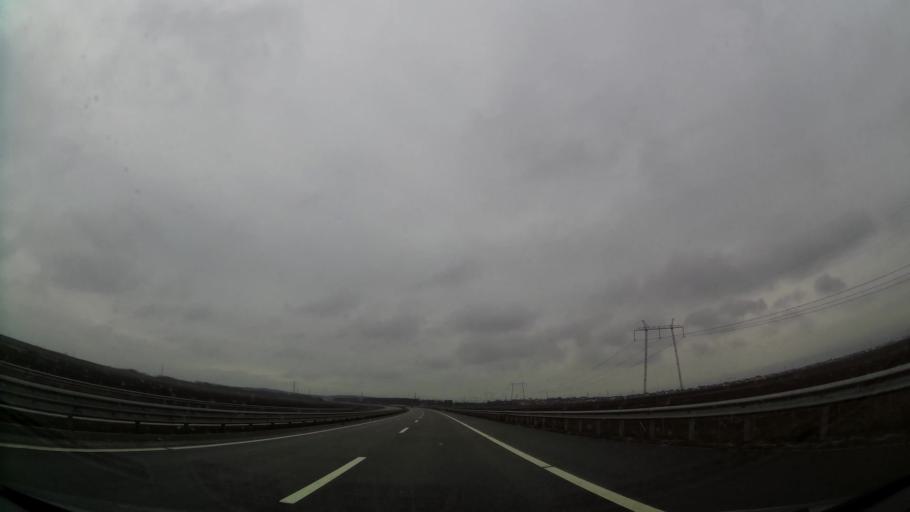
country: XK
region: Ferizaj
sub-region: Komuna e Ferizajt
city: Ferizaj
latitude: 42.3889
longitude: 21.1998
